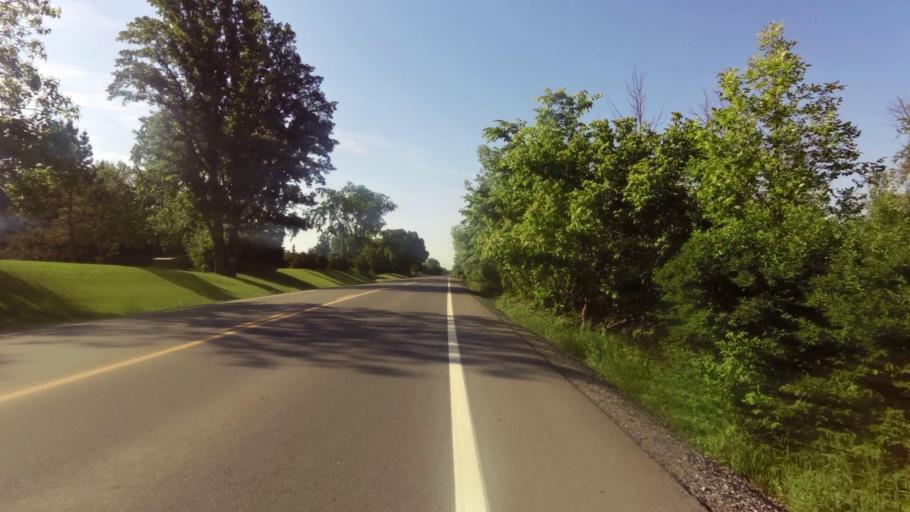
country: CA
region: Ontario
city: Ottawa
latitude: 45.2645
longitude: -75.5718
